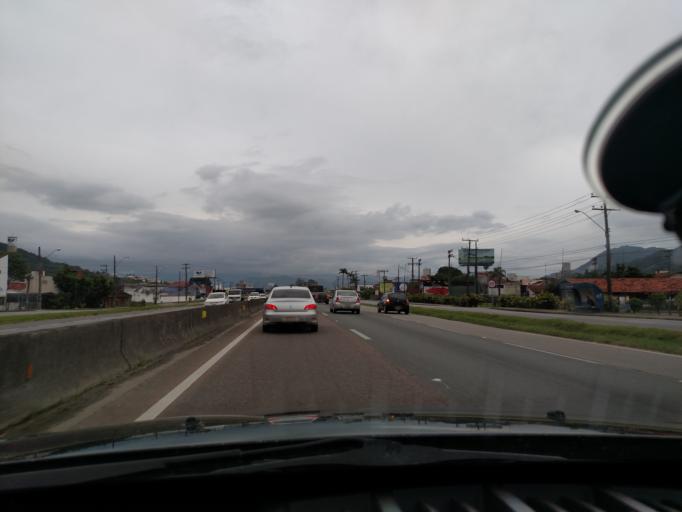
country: BR
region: Santa Catarina
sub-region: Biguacu
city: Biguacu
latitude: -27.5022
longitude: -48.6528
